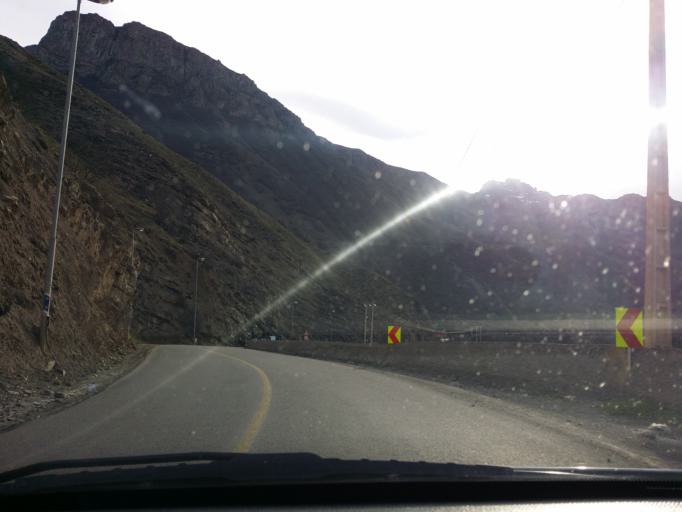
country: IR
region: Mazandaran
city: Chalus
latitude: 36.2475
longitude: 51.2950
